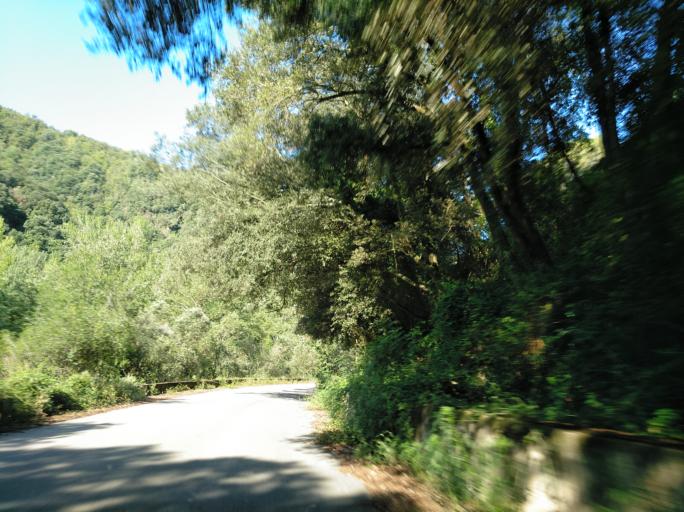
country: ES
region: Catalonia
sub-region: Provincia de Girona
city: Susqueda
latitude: 41.9846
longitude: 2.5517
